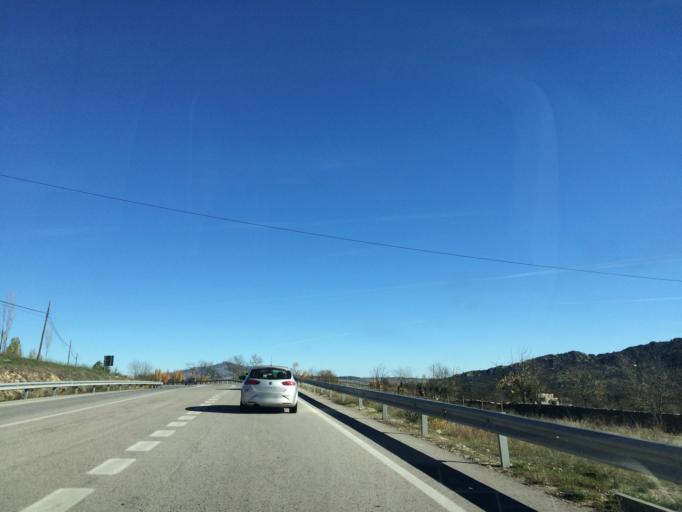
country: ES
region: Madrid
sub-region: Provincia de Madrid
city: Manzanares el Real
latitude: 40.7240
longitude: -3.8737
